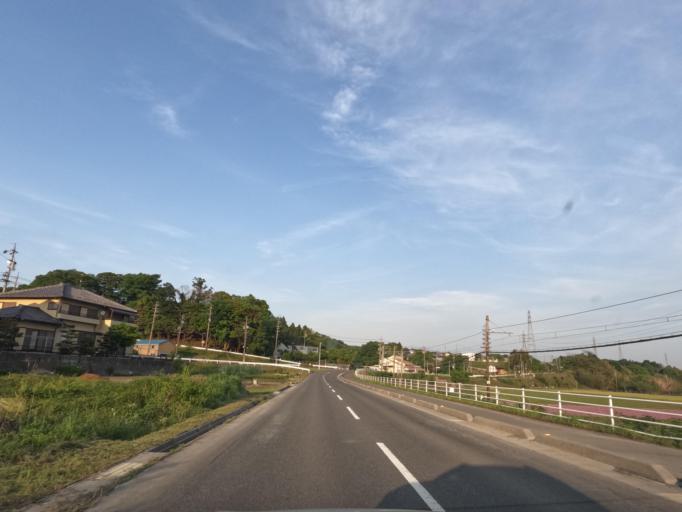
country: JP
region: Mie
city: Komono
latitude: 35.1467
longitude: 136.5222
